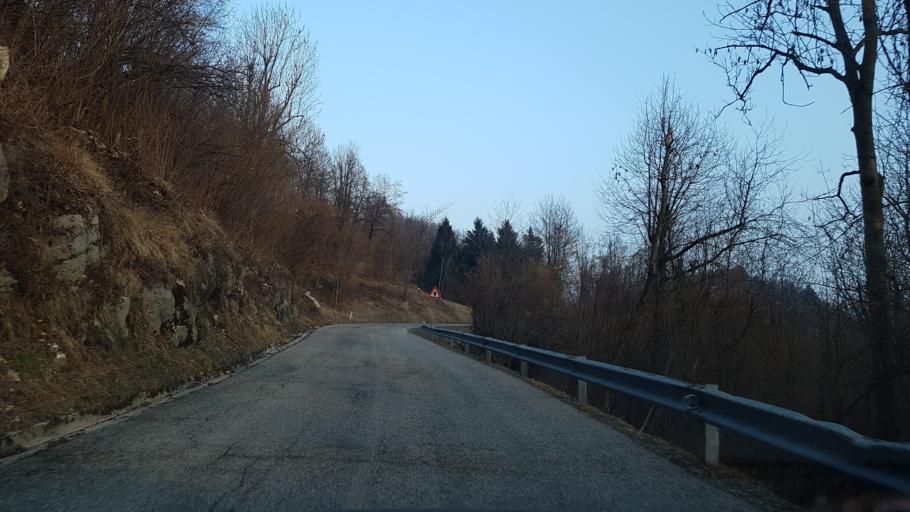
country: IT
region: Friuli Venezia Giulia
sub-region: Provincia di Udine
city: Taipana
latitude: 46.2604
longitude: 13.3468
